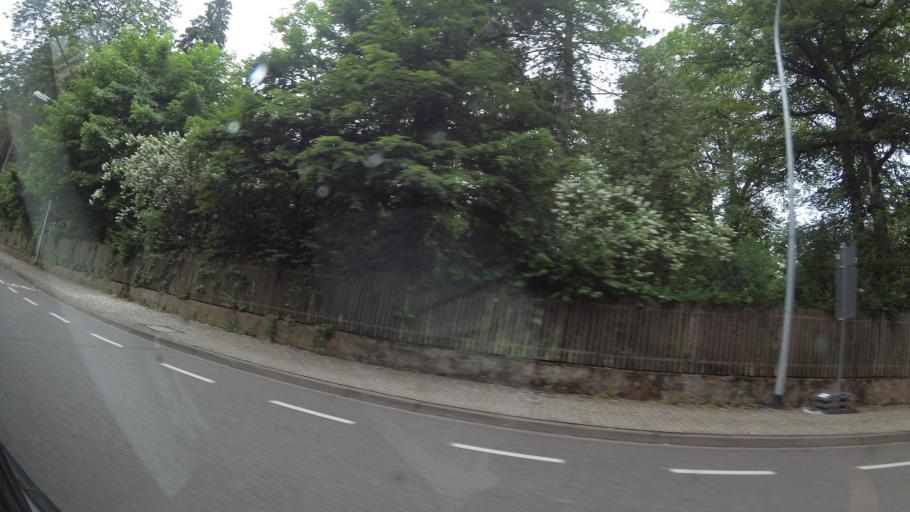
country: DE
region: Saarland
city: Saarbrucken
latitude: 49.2514
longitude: 6.9541
